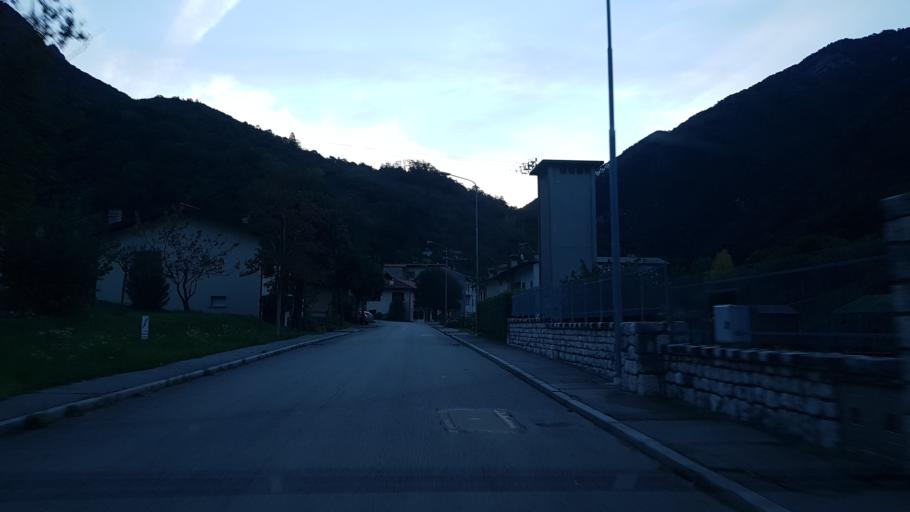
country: IT
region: Friuli Venezia Giulia
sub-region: Provincia di Udine
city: Venzone
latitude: 46.3362
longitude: 13.1427
